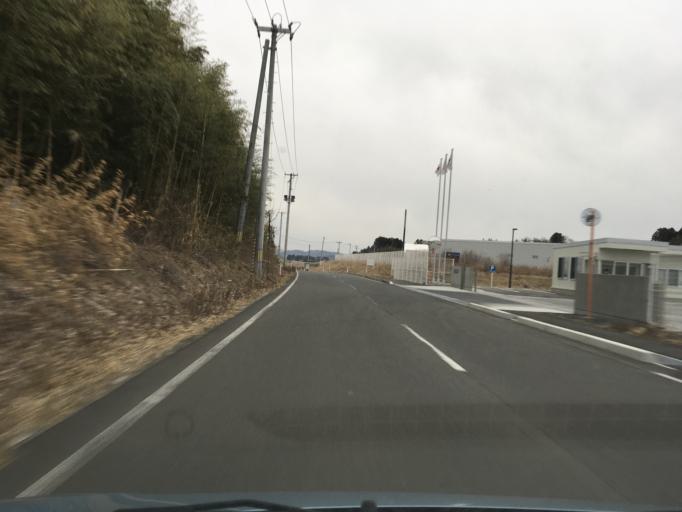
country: JP
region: Miyagi
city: Wakuya
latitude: 38.7008
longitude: 141.1678
